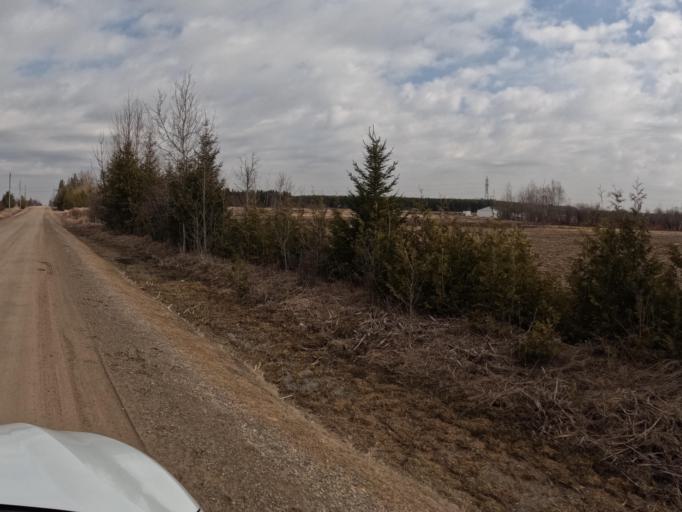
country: CA
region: Ontario
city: Orangeville
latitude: 43.9297
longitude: -80.2200
